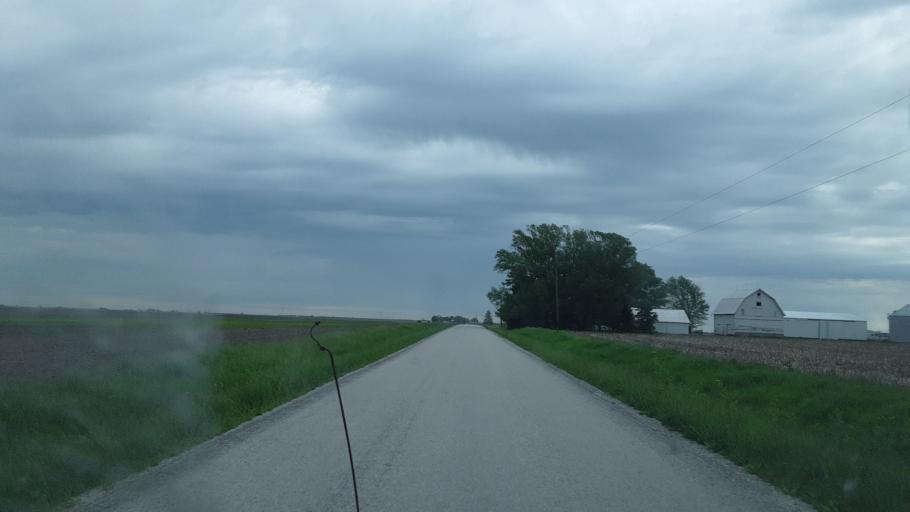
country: US
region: Illinois
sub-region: McDonough County
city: Bushnell
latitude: 40.3808
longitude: -90.5150
